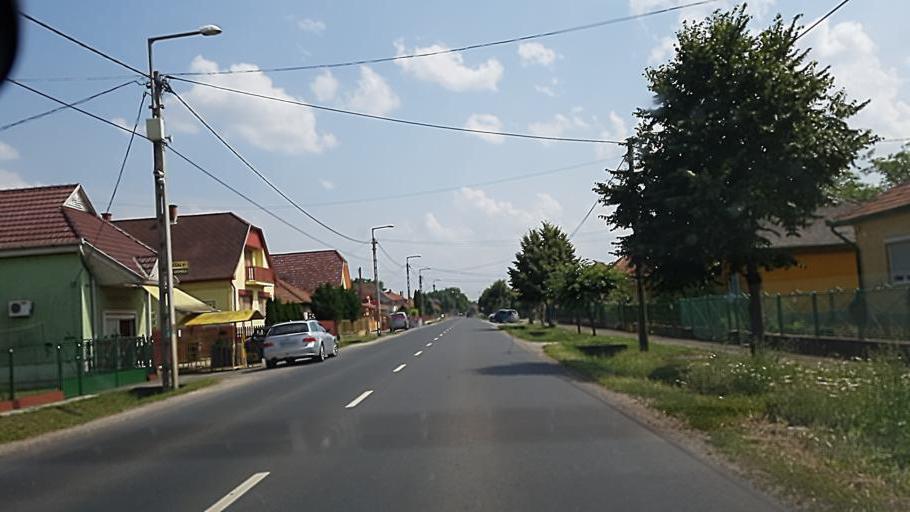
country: HU
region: Heves
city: Besenyotelek
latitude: 47.7088
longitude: 20.4253
